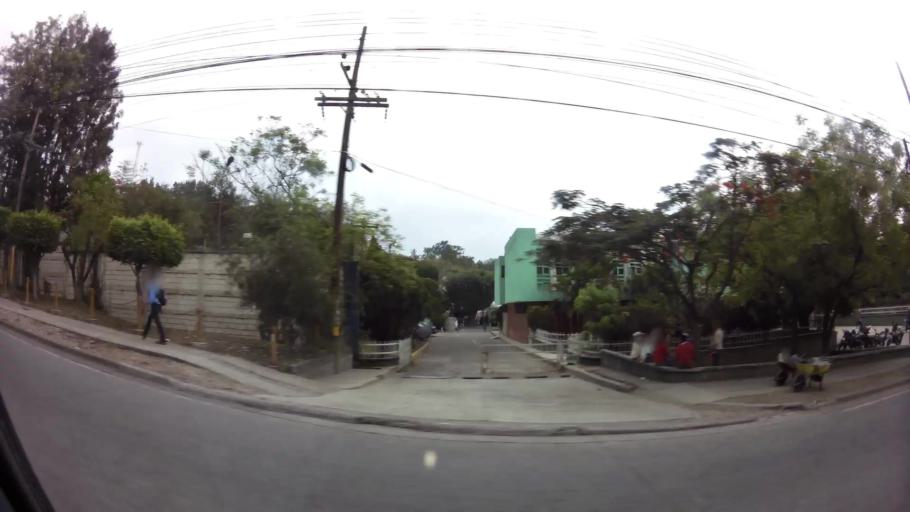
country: HN
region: Francisco Morazan
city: Tegucigalpa
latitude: 14.1026
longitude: -87.2321
